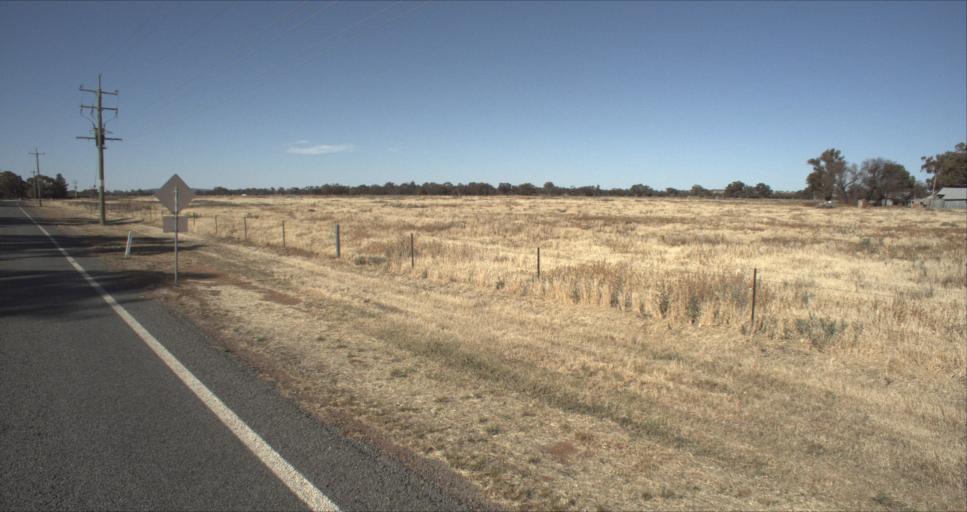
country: AU
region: New South Wales
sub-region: Leeton
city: Leeton
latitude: -34.6243
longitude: 146.3950
